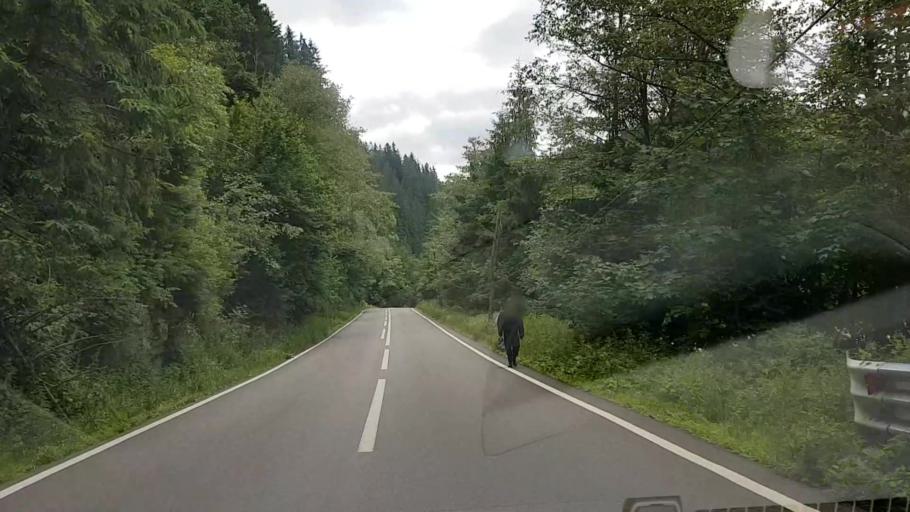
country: RO
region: Suceava
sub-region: Comuna Crucea
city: Crucea
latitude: 47.3669
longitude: 25.5907
